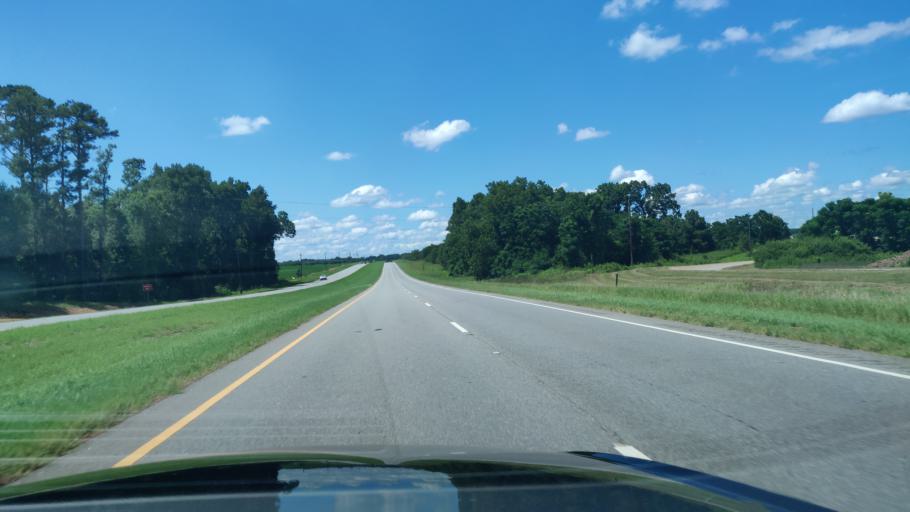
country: US
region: Georgia
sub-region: Terrell County
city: Dawson
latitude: 31.8375
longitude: -84.4679
